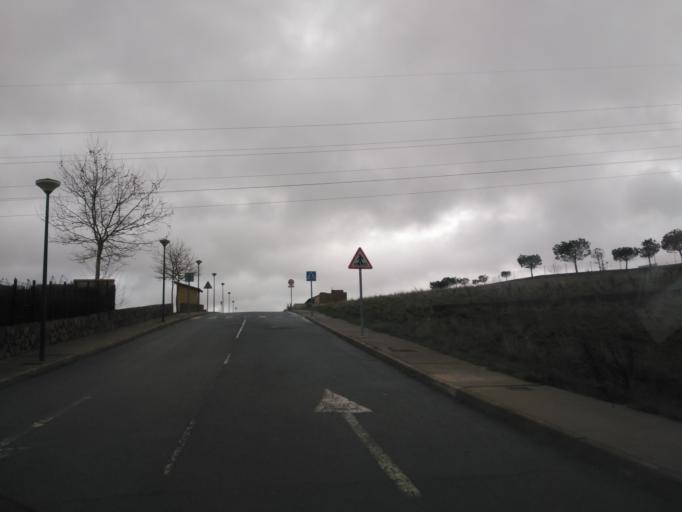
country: ES
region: Castille and Leon
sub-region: Provincia de Salamanca
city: Villamayor
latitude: 40.9806
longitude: -5.6978
